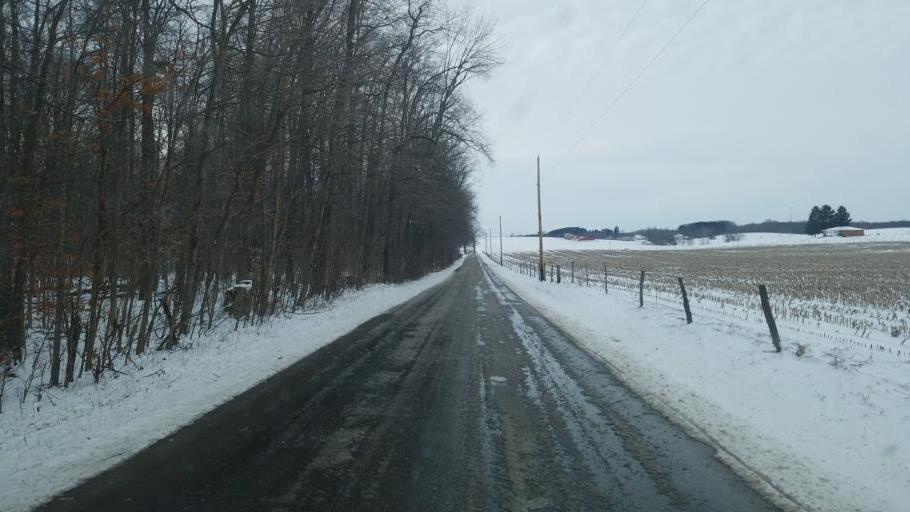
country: US
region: Ohio
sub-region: Knox County
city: Fredericktown
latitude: 40.5196
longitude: -82.6241
